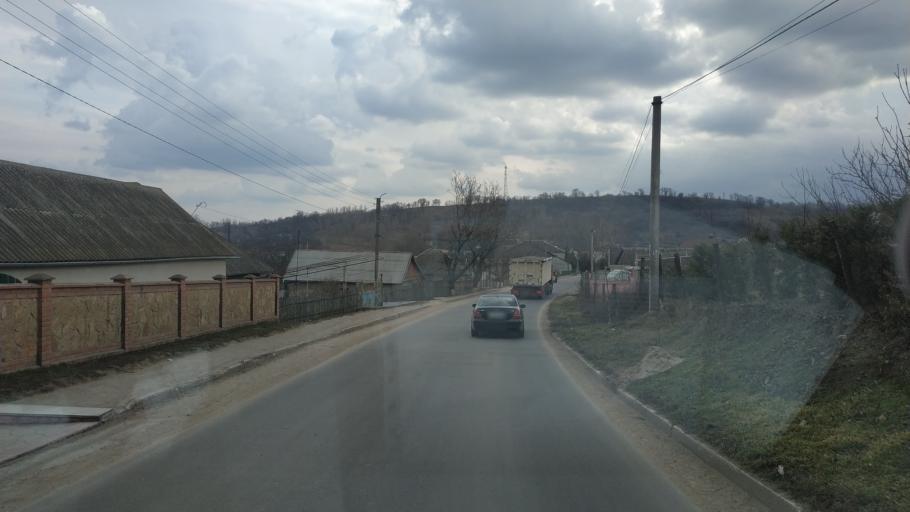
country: MD
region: Anenii Noi
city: Varnita
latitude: 46.8436
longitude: 29.3577
